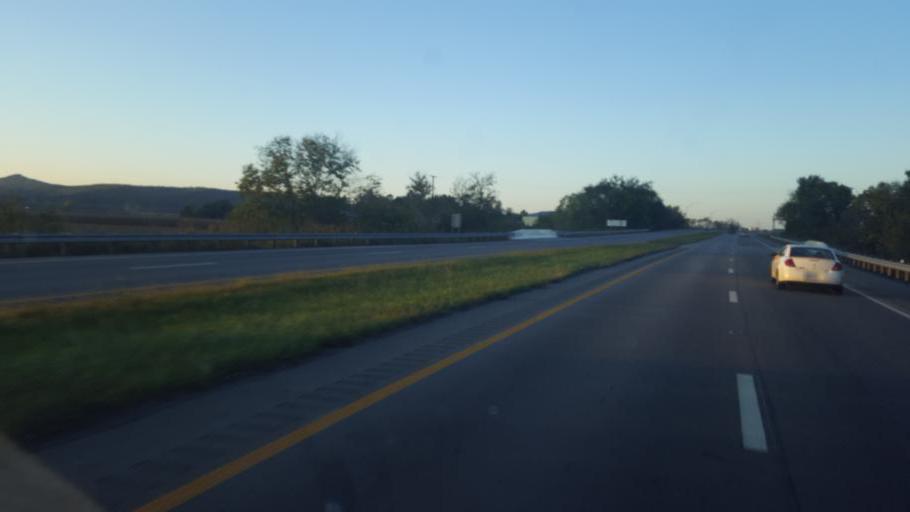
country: US
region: Ohio
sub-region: Pike County
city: Piketon
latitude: 39.0397
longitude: -83.0278
